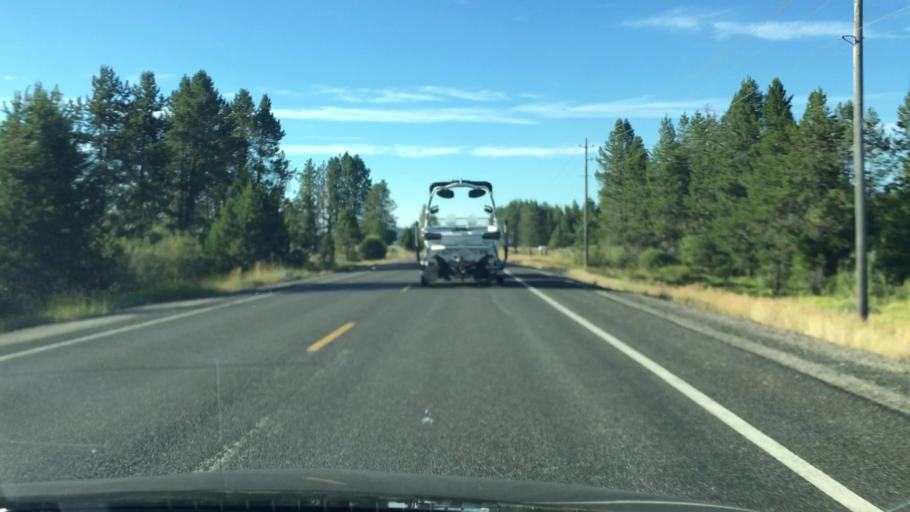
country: US
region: Idaho
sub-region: Valley County
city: Cascade
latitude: 44.4685
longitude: -115.9991
